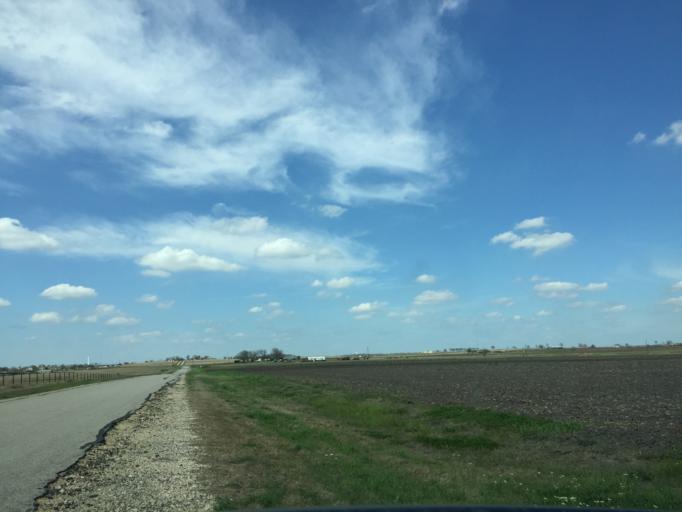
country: US
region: Texas
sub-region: Milam County
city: Thorndale
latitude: 30.5489
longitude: -97.2965
